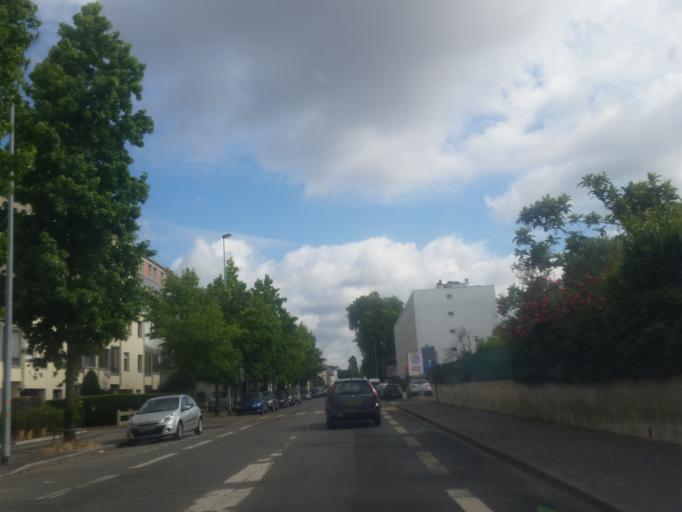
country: FR
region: Pays de la Loire
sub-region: Departement de la Loire-Atlantique
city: Saint-Sebastien-sur-Loire
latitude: 47.2310
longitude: -1.5231
